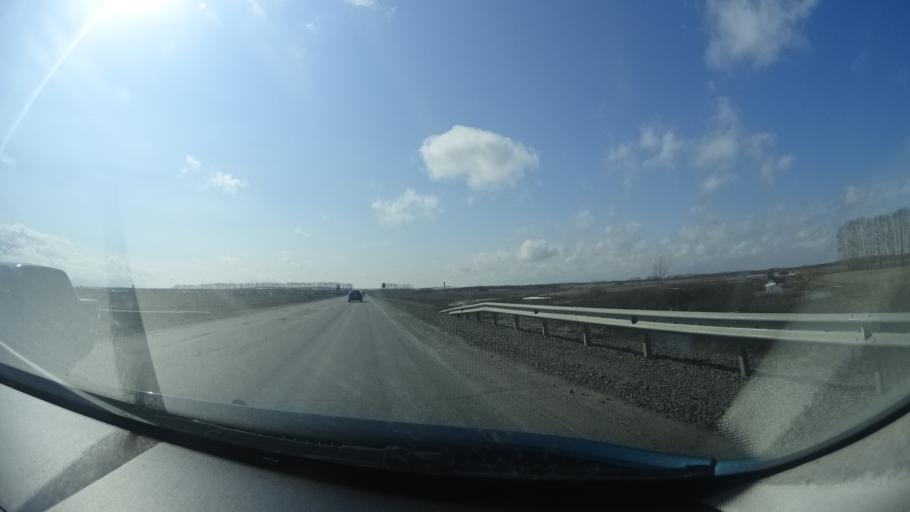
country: RU
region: Bashkortostan
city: Mikhaylovka
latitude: 54.9314
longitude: 55.7422
